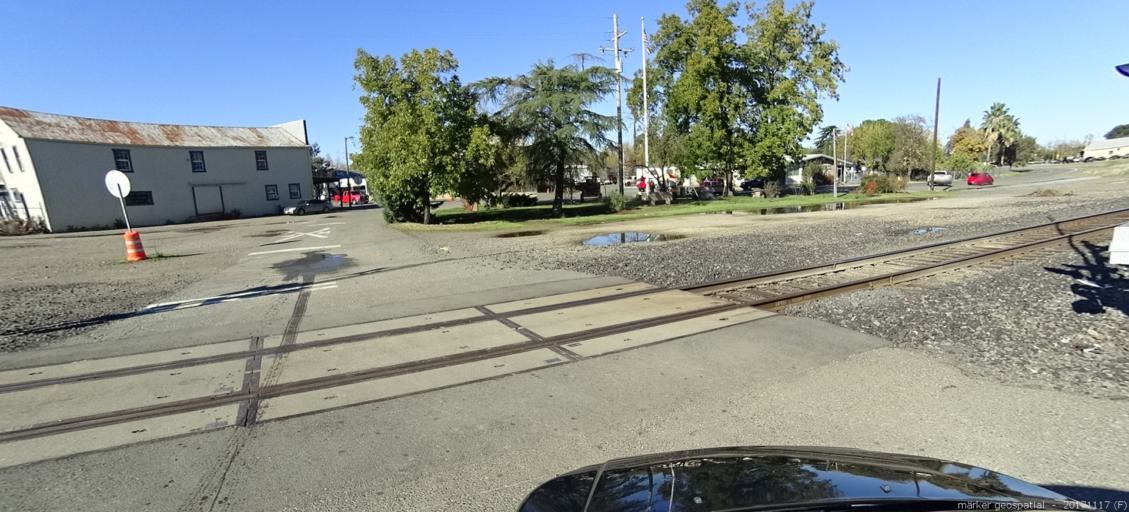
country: US
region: California
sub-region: Shasta County
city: Cottonwood
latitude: 40.3815
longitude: -122.2797
